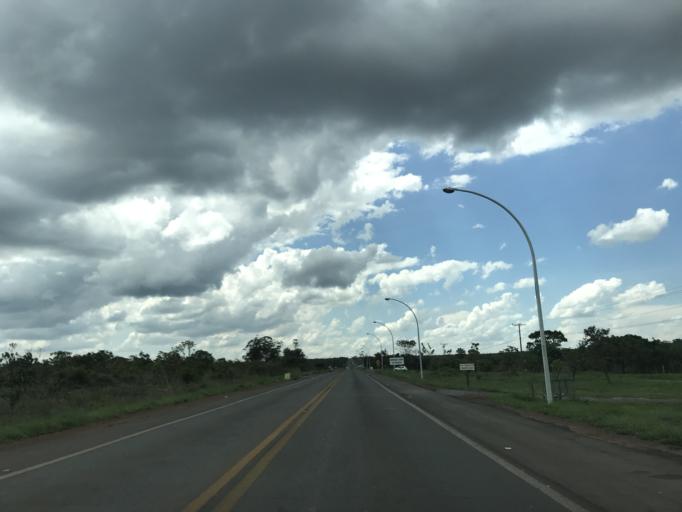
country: BR
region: Federal District
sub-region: Brasilia
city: Brasilia
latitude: -15.6844
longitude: -47.8642
